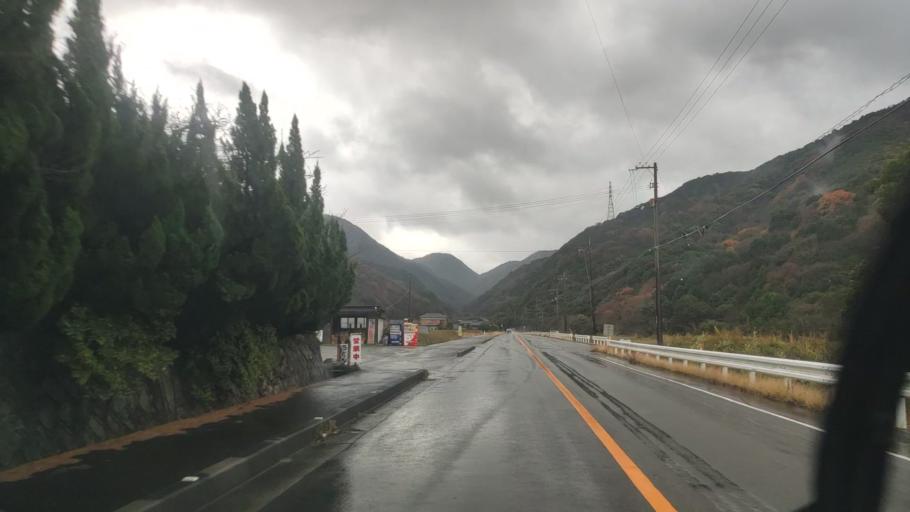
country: JP
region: Tokushima
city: Kamojimacho-jogejima
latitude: 34.1954
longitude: 134.3329
